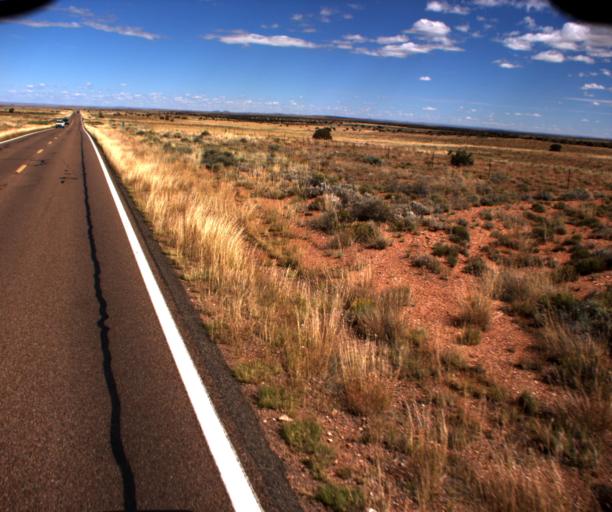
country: US
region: Arizona
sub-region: Navajo County
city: Holbrook
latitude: 34.7302
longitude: -110.2834
